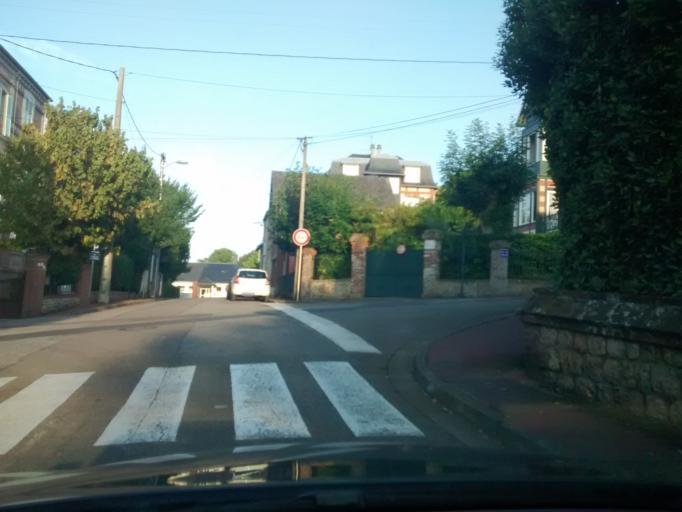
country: FR
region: Lower Normandy
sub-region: Departement du Calvados
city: Villers-sur-Mer
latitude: 49.3206
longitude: -0.0043
